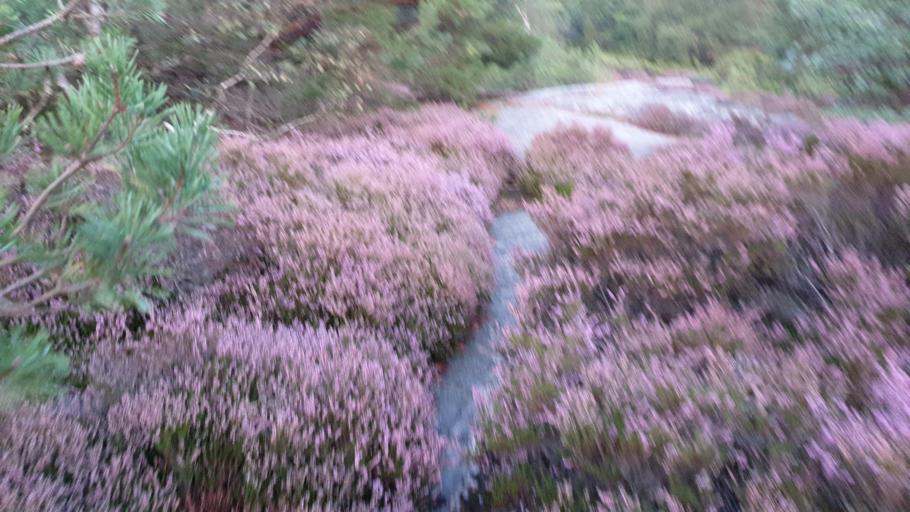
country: SE
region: Vaestra Goetaland
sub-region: Goteborg
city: Billdal
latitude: 57.5919
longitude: 11.9101
